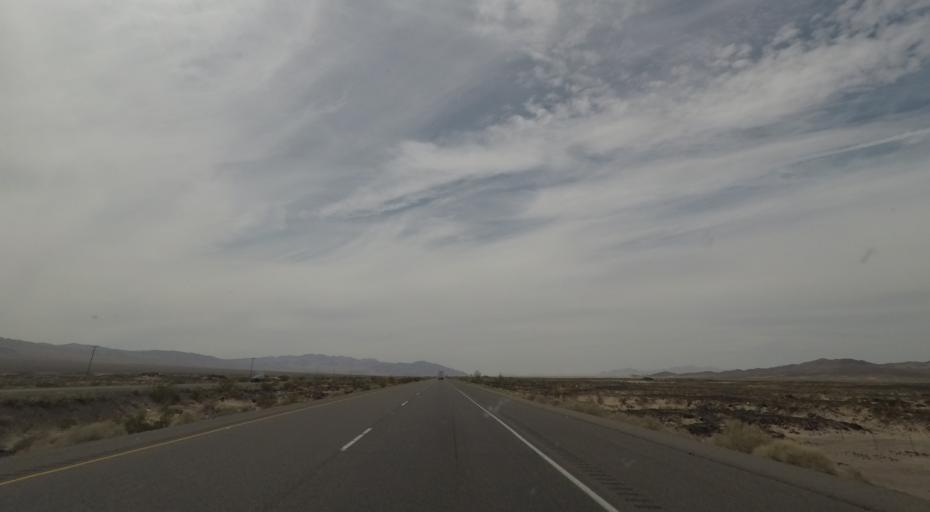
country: US
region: California
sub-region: San Bernardino County
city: Fort Irwin
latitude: 34.7904
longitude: -116.4722
